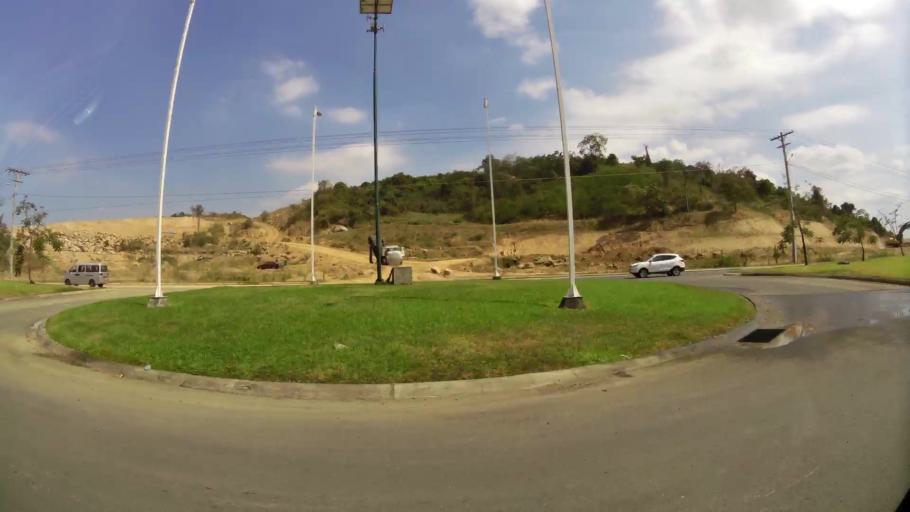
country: EC
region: Guayas
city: El Triunfo
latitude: -2.0303
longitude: -79.9035
